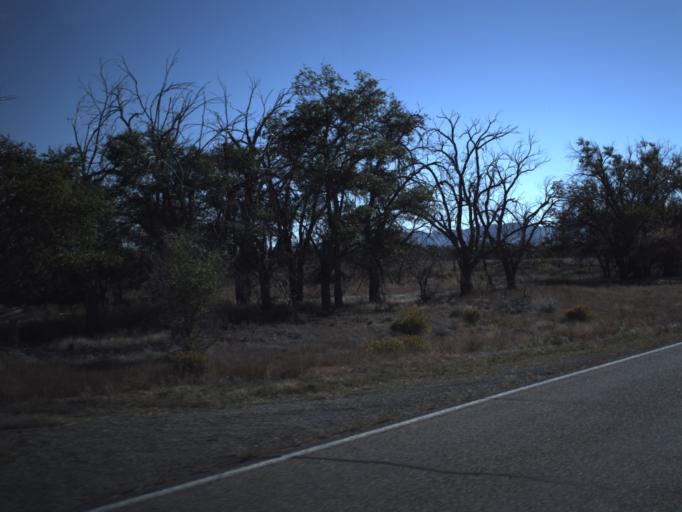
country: US
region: Utah
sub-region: Washington County
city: Enterprise
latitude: 37.7194
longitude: -113.6838
